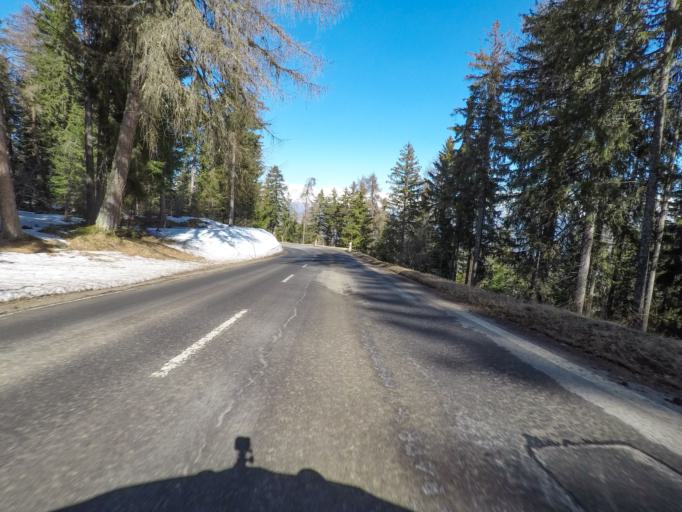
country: CH
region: Valais
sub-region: Herens District
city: Vex
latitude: 46.1959
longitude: 7.3823
